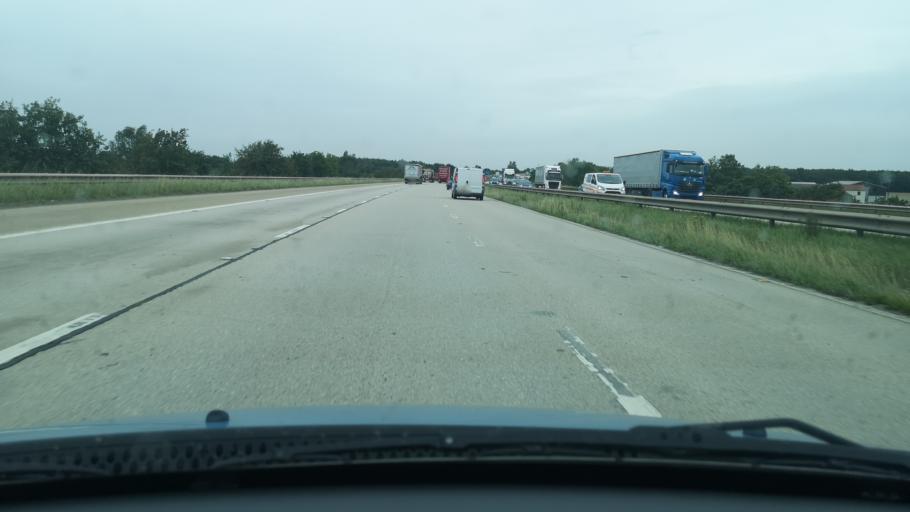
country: GB
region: England
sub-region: Doncaster
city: Hatfield
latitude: 53.6031
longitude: -0.9909
